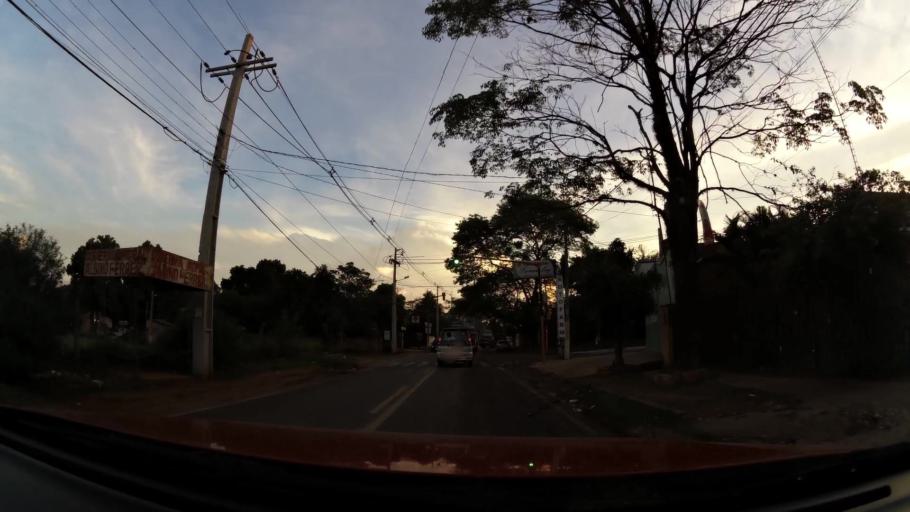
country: PY
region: Central
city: San Lorenzo
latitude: -25.3656
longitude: -57.4906
